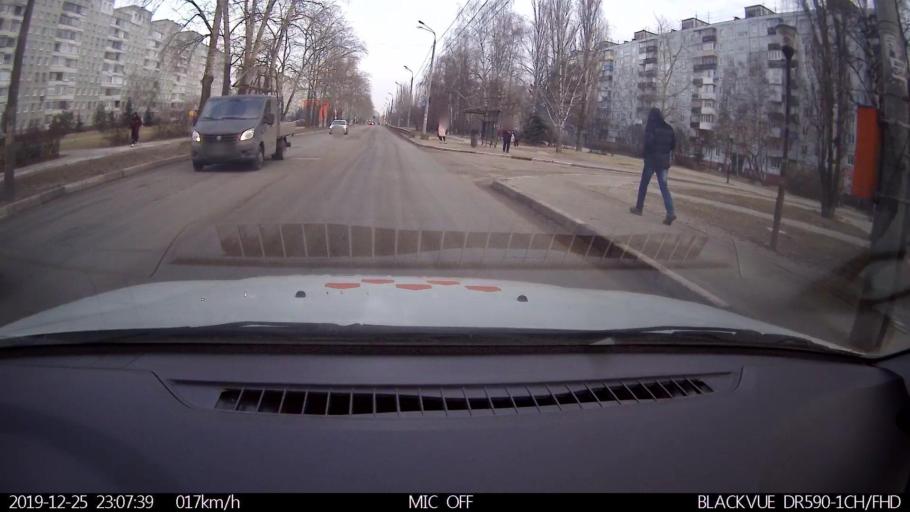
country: RU
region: Nizjnij Novgorod
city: Gorbatovka
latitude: 56.3618
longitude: 43.8097
